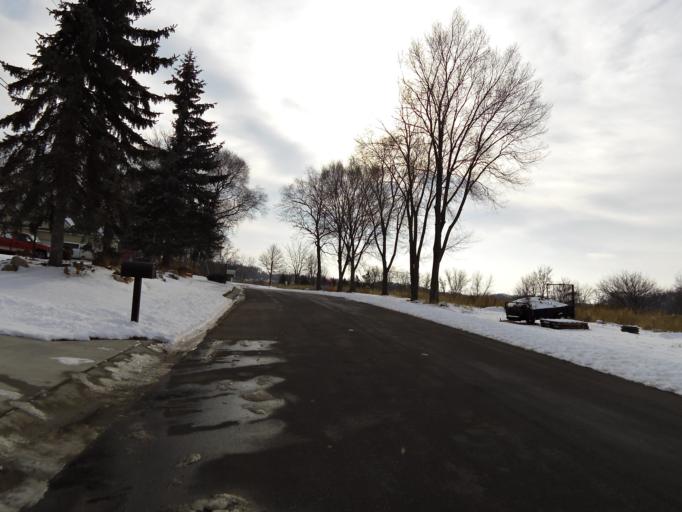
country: US
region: Minnesota
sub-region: Scott County
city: Prior Lake
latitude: 44.6996
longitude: -93.4886
